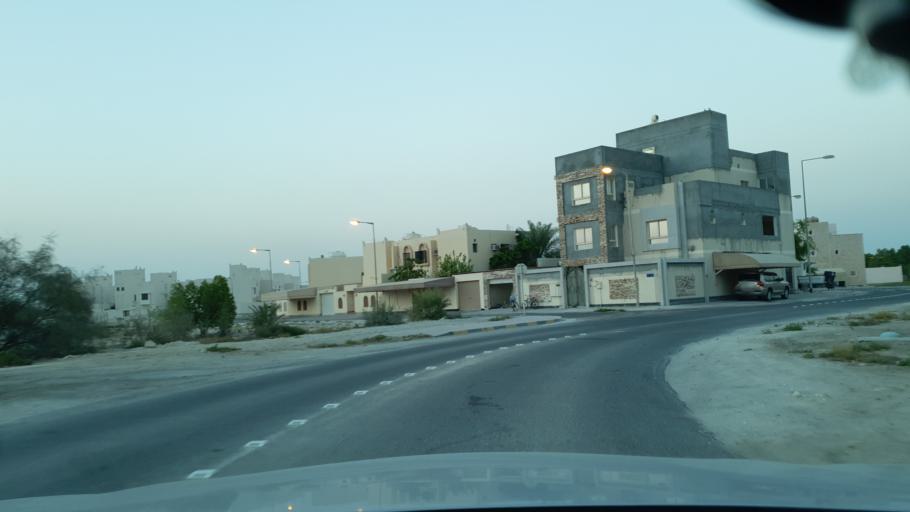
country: BH
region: Central Governorate
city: Dar Kulayb
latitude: 25.9774
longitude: 50.6147
